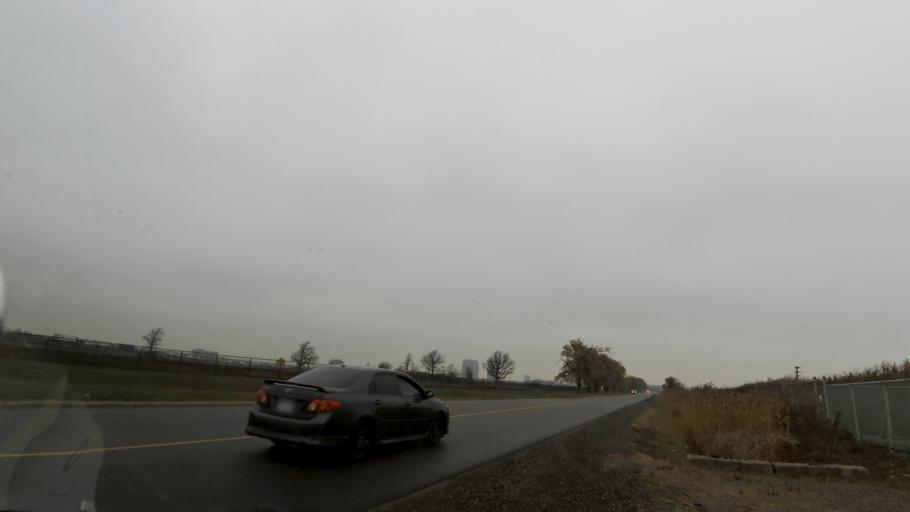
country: CA
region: Ontario
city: Etobicoke
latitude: 43.7086
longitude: -79.6117
